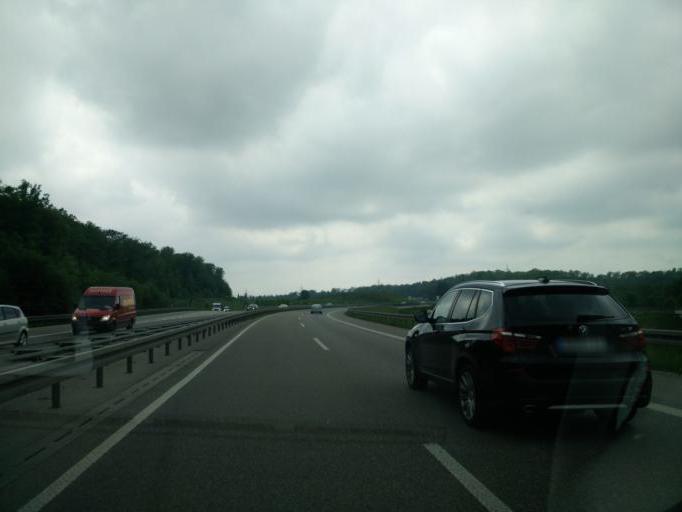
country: DE
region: Baden-Wuerttemberg
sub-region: Tuebingen Region
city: Metzingen
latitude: 48.5285
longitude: 9.2648
